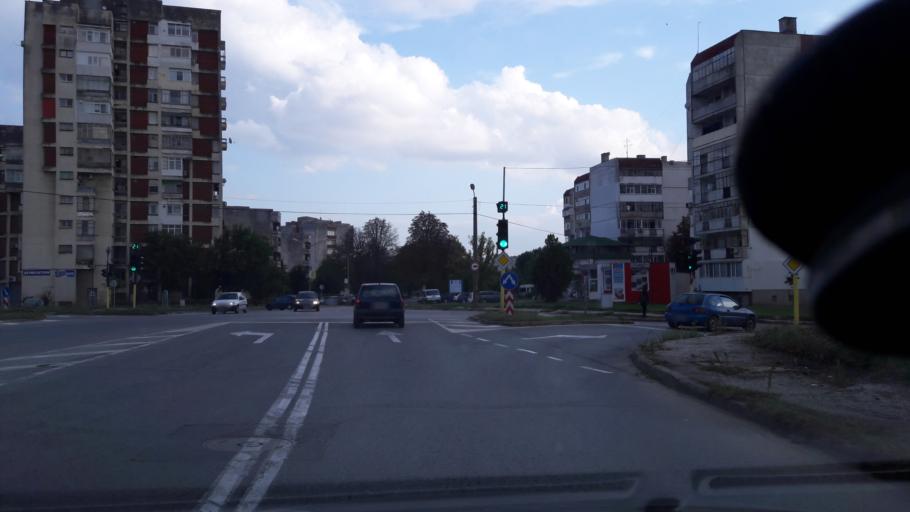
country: BG
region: Razgrad
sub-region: Obshtina Razgrad
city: Razgrad
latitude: 43.5345
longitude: 26.5221
